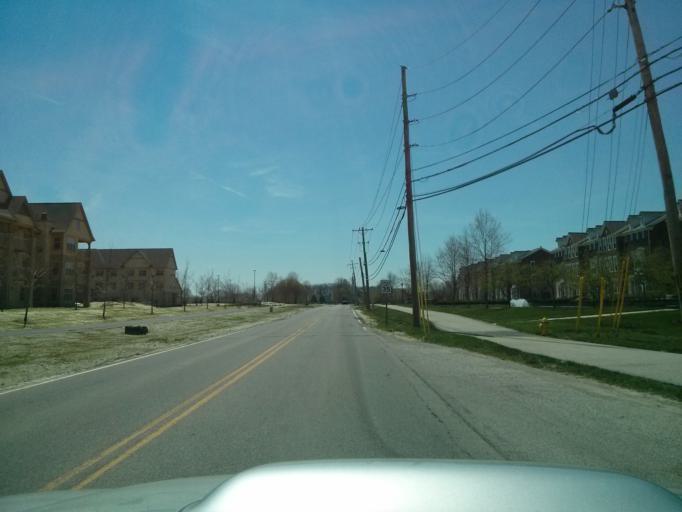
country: US
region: Indiana
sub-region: Hamilton County
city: Carmel
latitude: 39.9608
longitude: -86.1412
